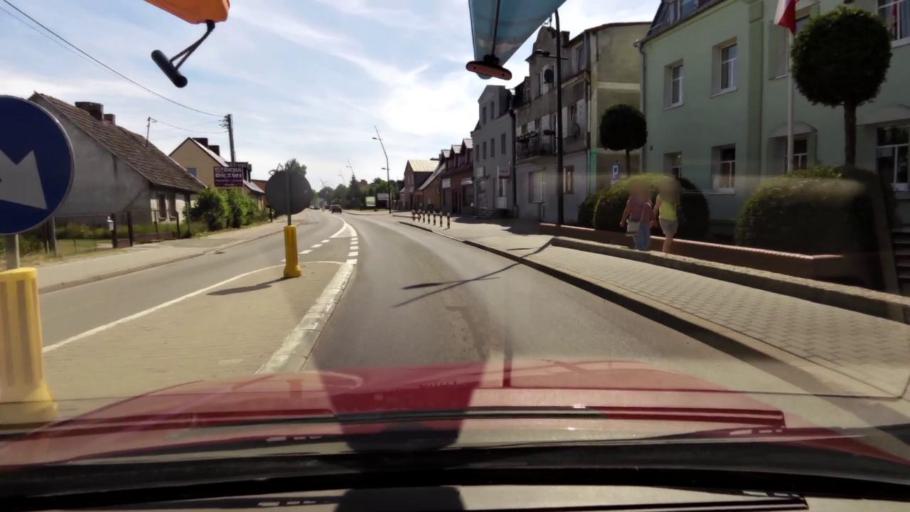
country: PL
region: Pomeranian Voivodeship
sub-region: Powiat slupski
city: Kobylnica
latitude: 54.4436
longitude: 17.0002
